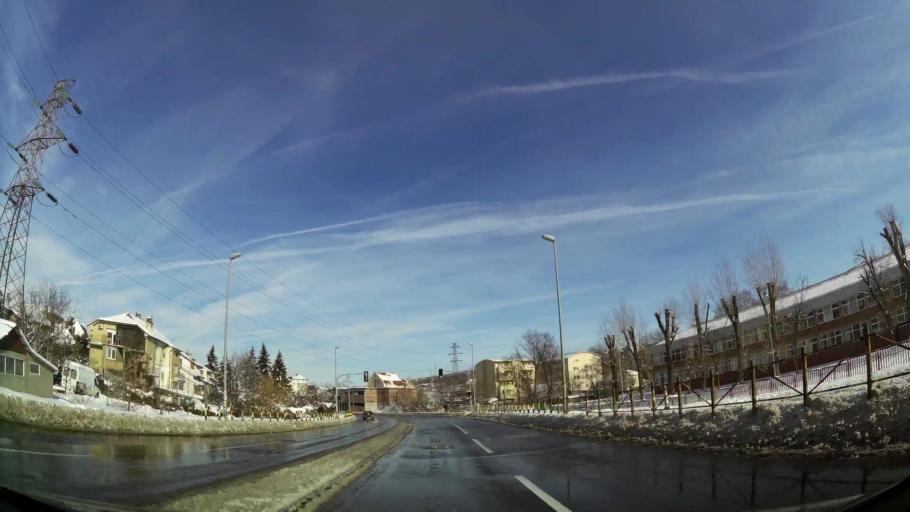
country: RS
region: Central Serbia
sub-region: Belgrade
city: Palilula
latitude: 44.7971
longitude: 20.5275
